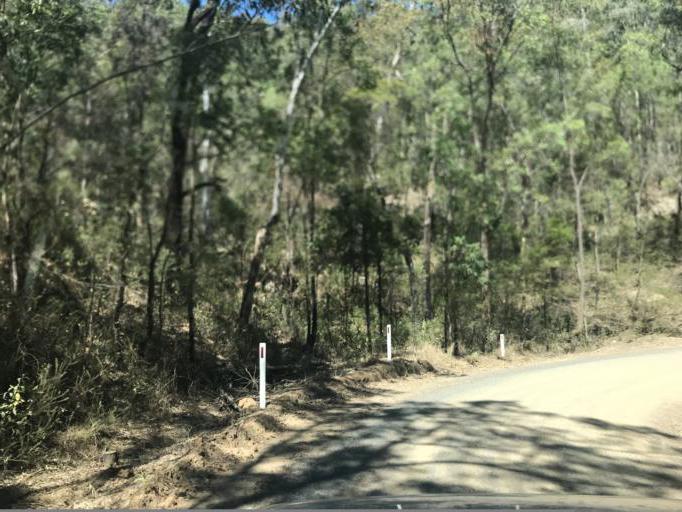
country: AU
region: New South Wales
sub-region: Wyong Shire
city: Little Jilliby
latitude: -33.1613
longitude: 151.0728
